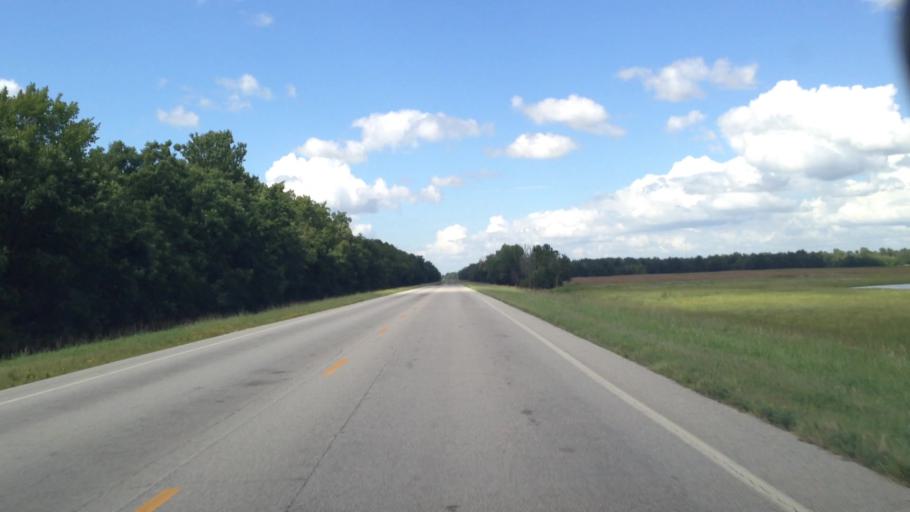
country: US
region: Kansas
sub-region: Labette County
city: Chetopa
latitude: 37.0636
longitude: -95.1028
